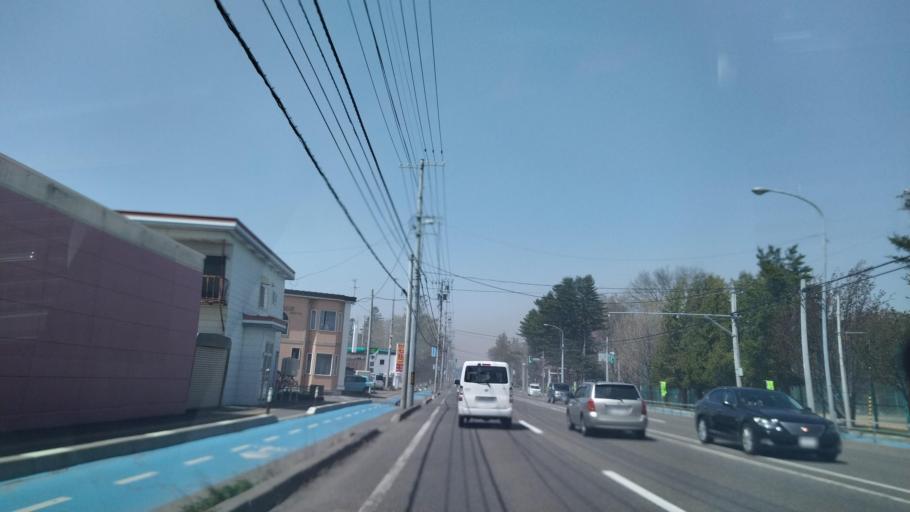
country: JP
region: Hokkaido
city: Obihiro
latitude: 42.9296
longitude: 143.2123
